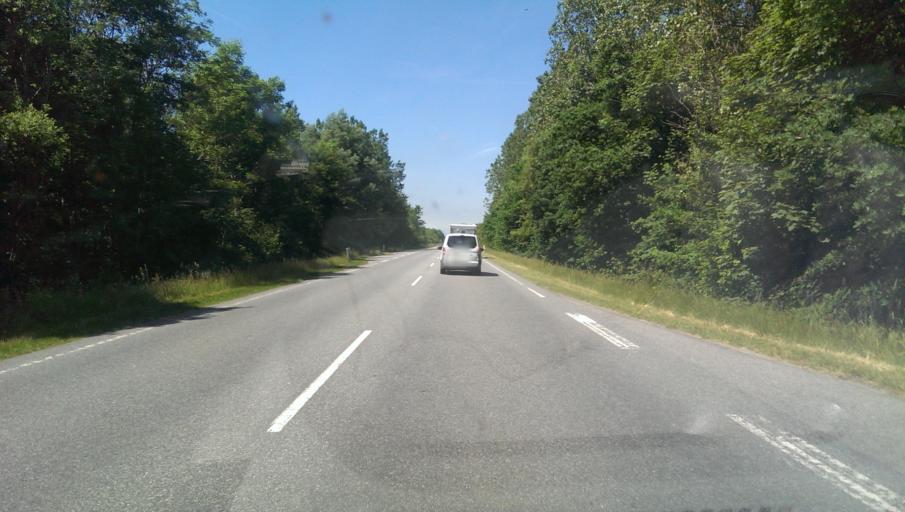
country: DK
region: South Denmark
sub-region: Esbjerg Kommune
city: Esbjerg
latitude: 55.5250
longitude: 8.4448
